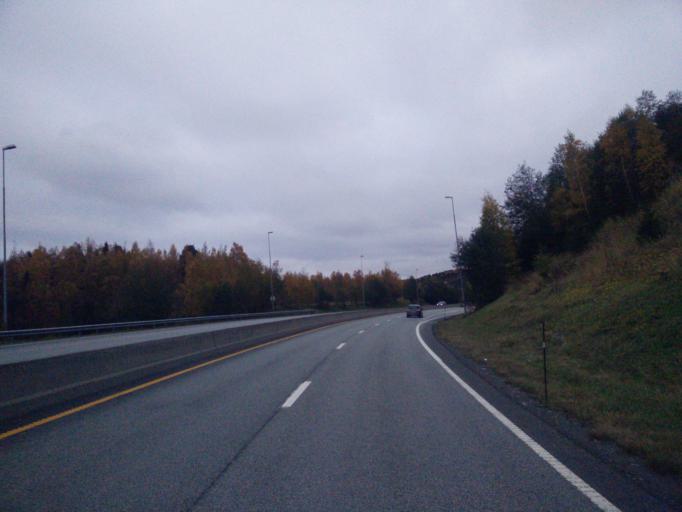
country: NO
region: Sor-Trondelag
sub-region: Malvik
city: Hommelvik
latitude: 63.4097
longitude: 10.8164
